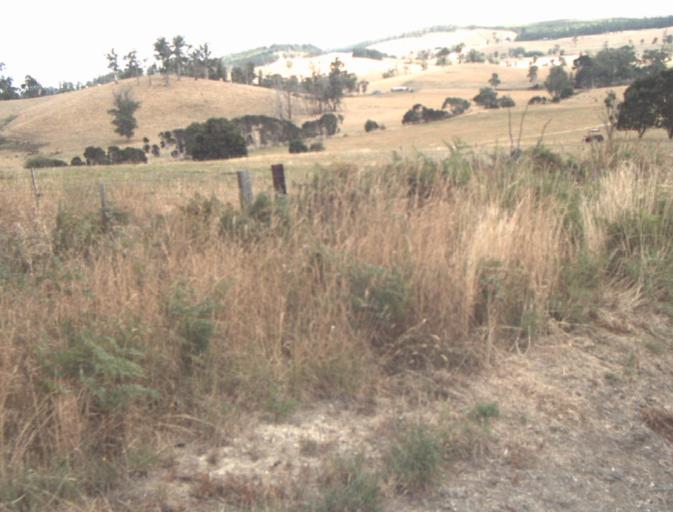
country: AU
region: Tasmania
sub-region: Launceston
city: Mayfield
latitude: -41.2151
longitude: 147.1073
